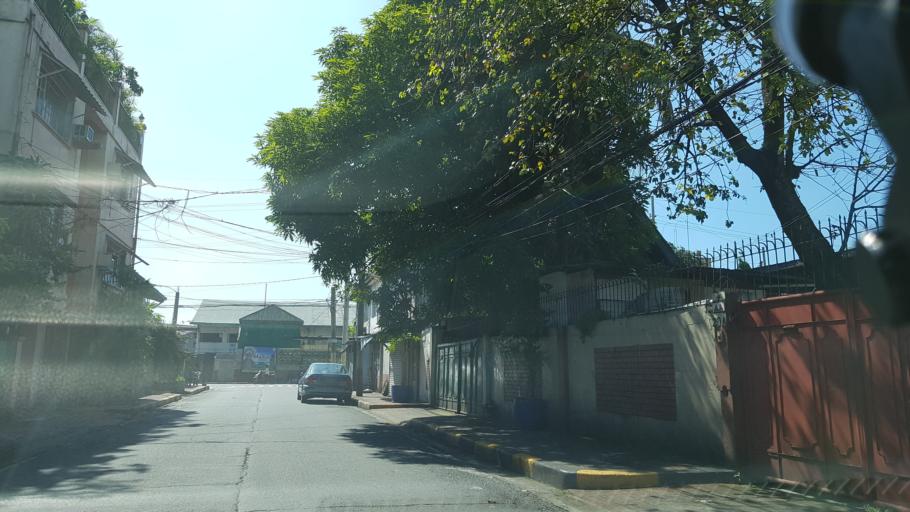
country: PH
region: Calabarzon
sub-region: Province of Rizal
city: Pateros
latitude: 14.5618
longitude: 121.0701
